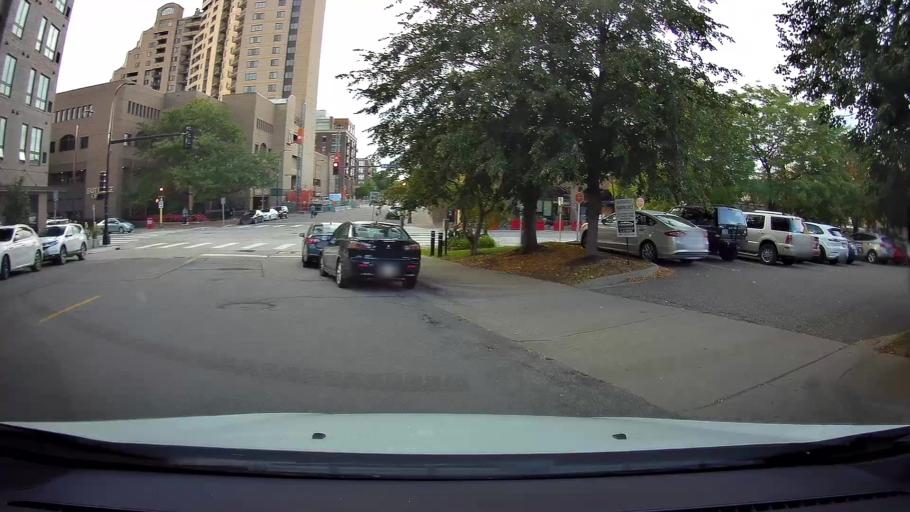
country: US
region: Minnesota
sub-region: Hennepin County
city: Minneapolis
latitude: 44.9870
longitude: -93.2575
